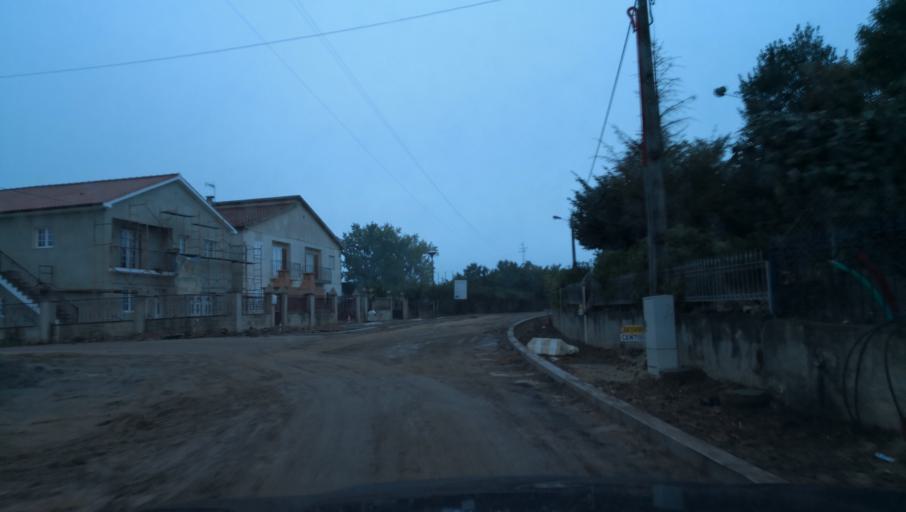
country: PT
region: Vila Real
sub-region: Sabrosa
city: Sabrosa
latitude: 41.2642
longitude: -7.6116
